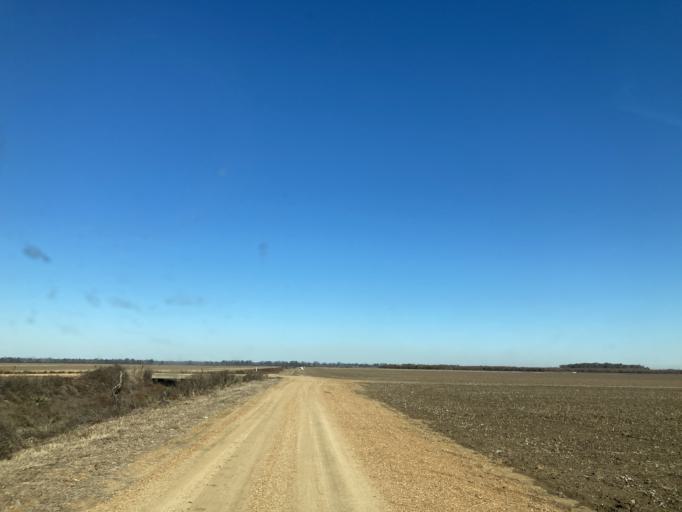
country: US
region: Mississippi
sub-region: Sharkey County
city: Rolling Fork
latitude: 32.8494
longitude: -90.6722
